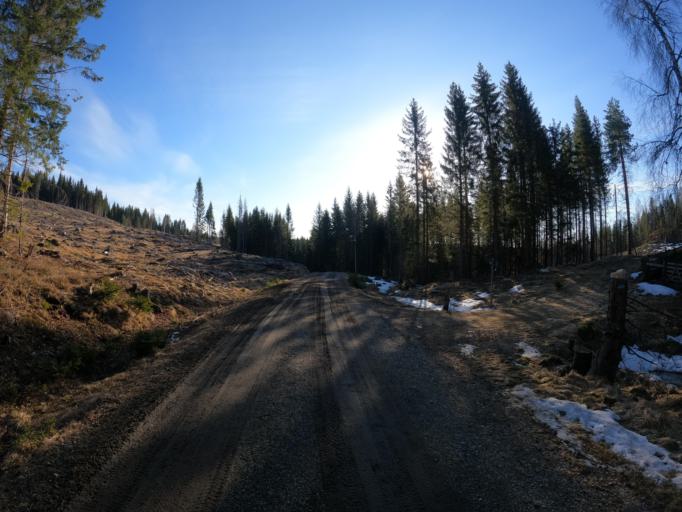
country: NO
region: Akershus
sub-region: Nittedal
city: Aneby
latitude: 60.1375
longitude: 10.9091
